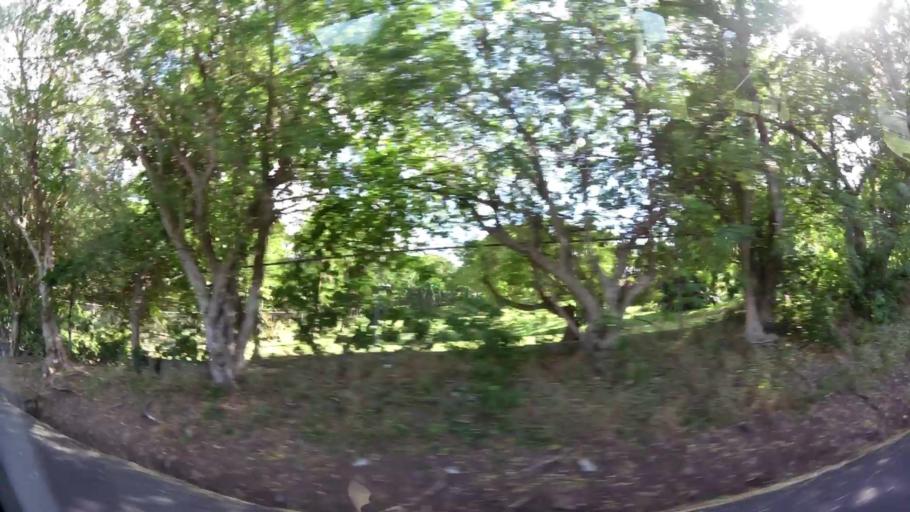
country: LC
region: Castries Quarter
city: Bisee
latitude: 14.0192
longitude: -60.9943
